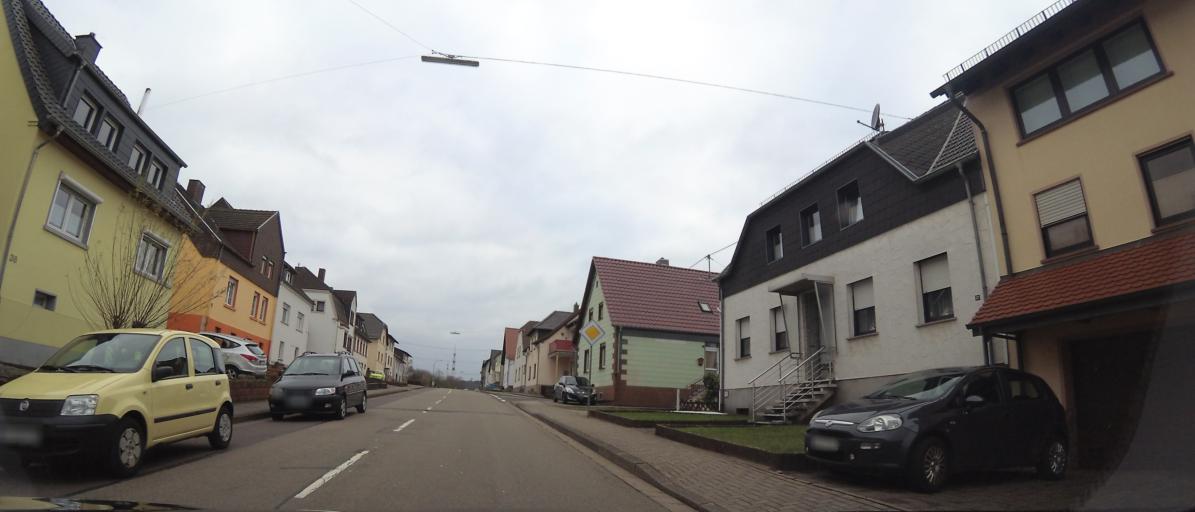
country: DE
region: Saarland
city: Illingen
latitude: 49.3689
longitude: 7.0137
